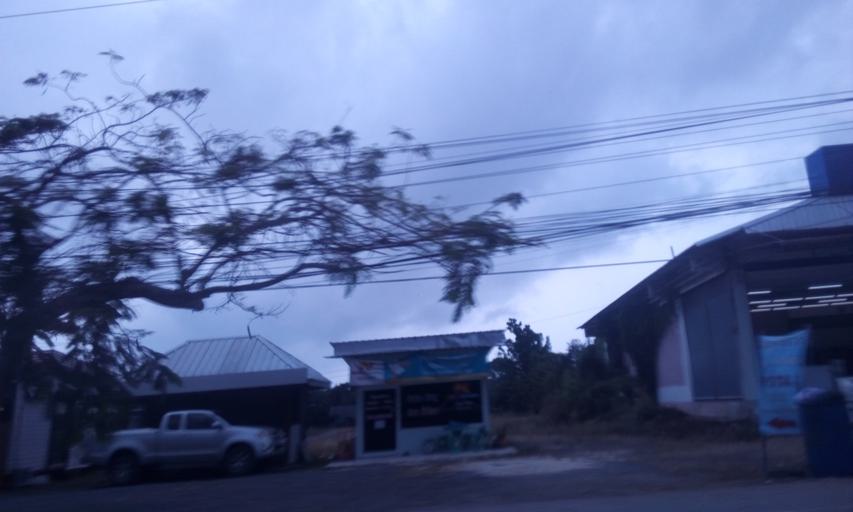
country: TH
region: Chanthaburi
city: Khlung
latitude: 12.4577
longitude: 102.2340
